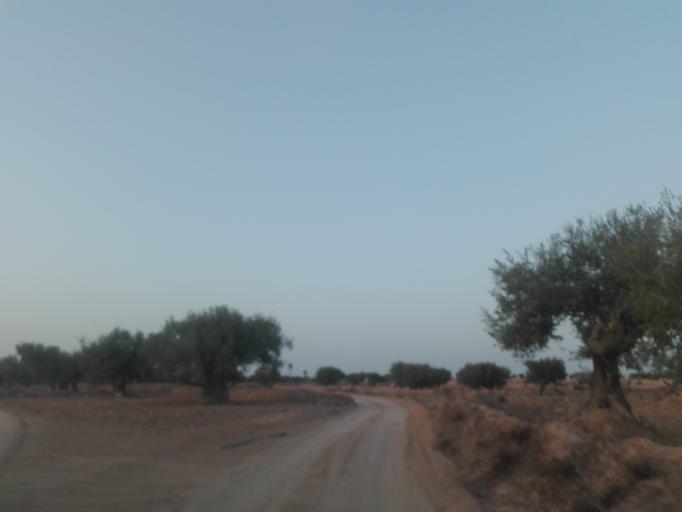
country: TN
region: Madanin
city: Houmt Souk
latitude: 33.7421
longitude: 10.7653
